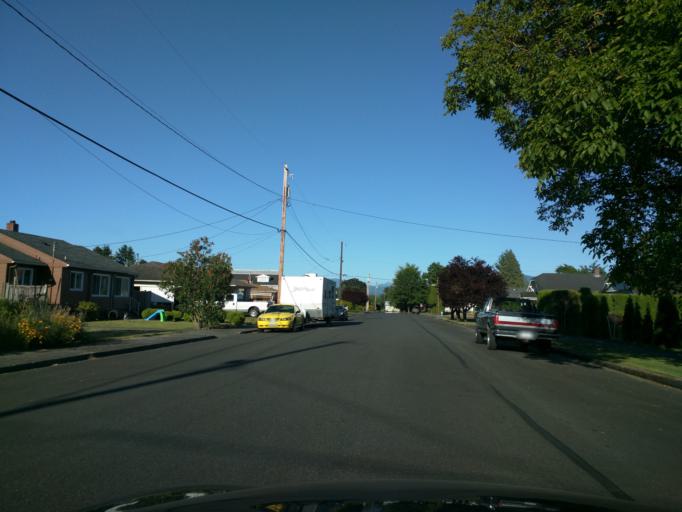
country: US
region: Washington
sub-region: Whatcom County
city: Lynden
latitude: 48.9379
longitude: -122.4664
